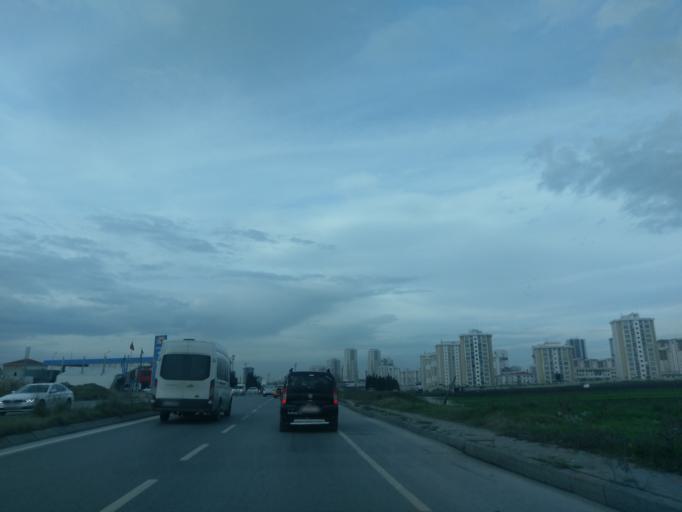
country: TR
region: Istanbul
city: Esenyurt
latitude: 41.0794
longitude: 28.6535
